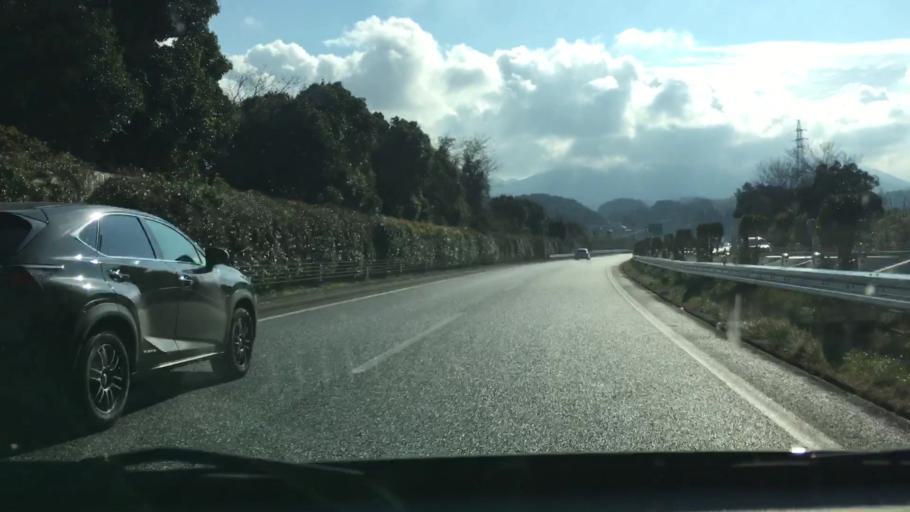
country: JP
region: Kumamoto
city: Matsubase
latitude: 32.5844
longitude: 130.7163
